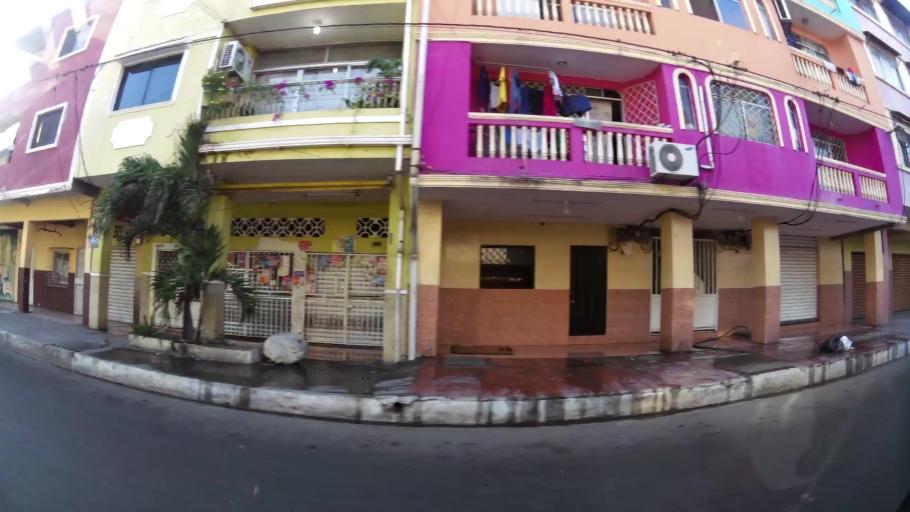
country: EC
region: Guayas
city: Eloy Alfaro
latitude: -2.1687
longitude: -79.8518
